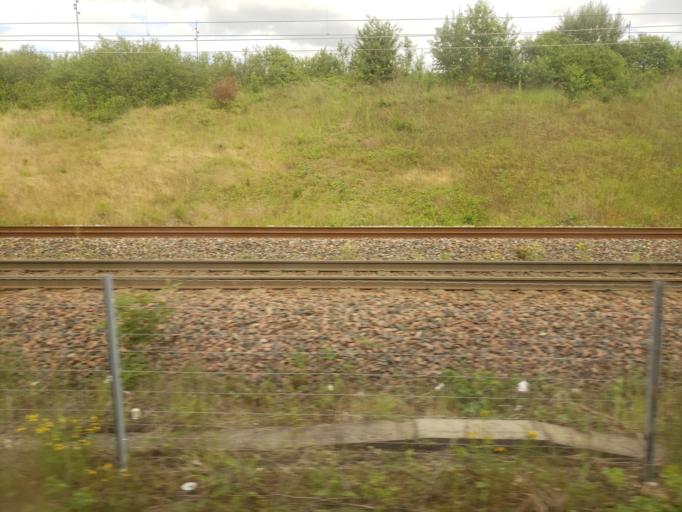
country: FR
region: Ile-de-France
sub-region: Departement de Seine-et-Marne
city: Serris
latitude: 48.8659
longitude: 2.7821
